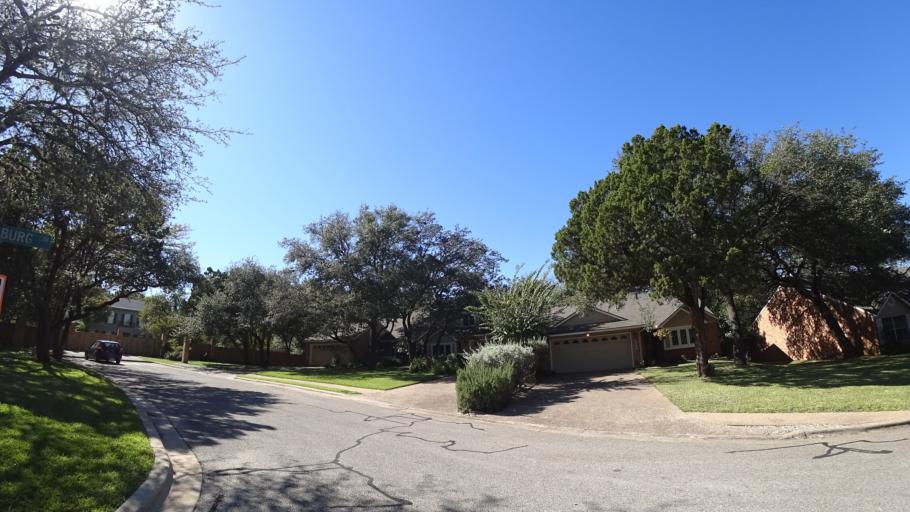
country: US
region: Texas
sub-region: Williamson County
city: Jollyville
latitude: 30.3661
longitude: -97.7549
